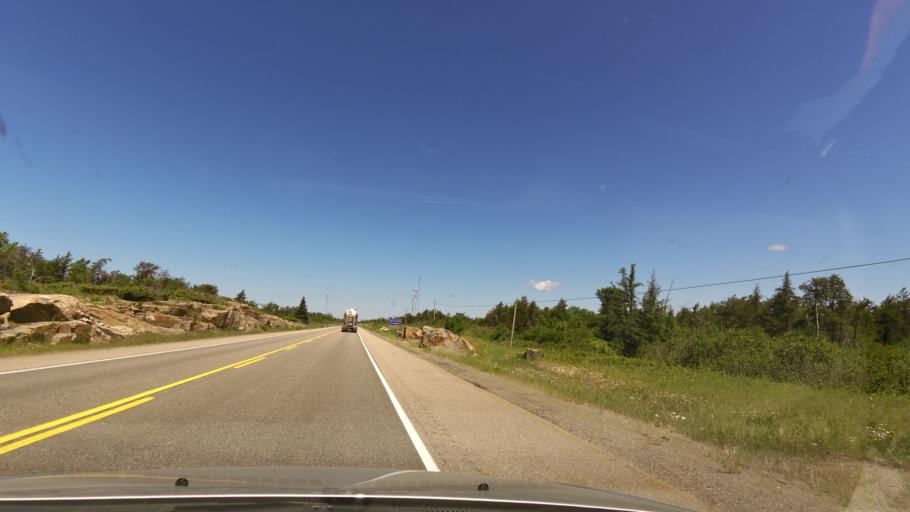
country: CA
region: Ontario
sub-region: Parry Sound District
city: Parry Sound
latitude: 45.7847
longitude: -80.5218
